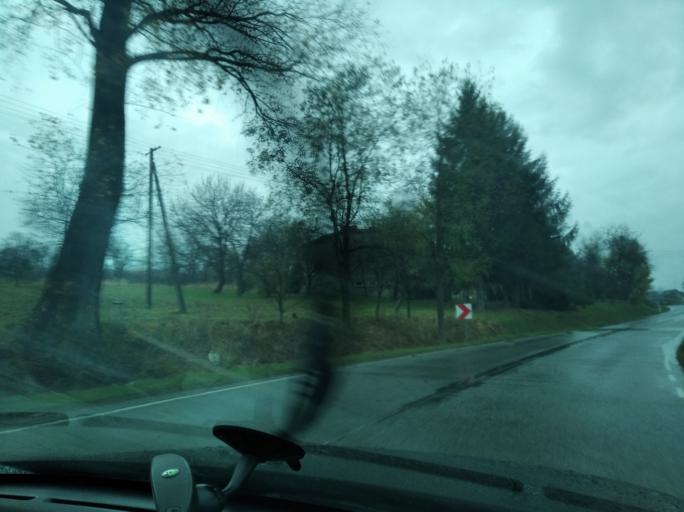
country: PL
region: Subcarpathian Voivodeship
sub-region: Powiat lancucki
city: Albigowa
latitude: 50.0092
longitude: 22.2162
